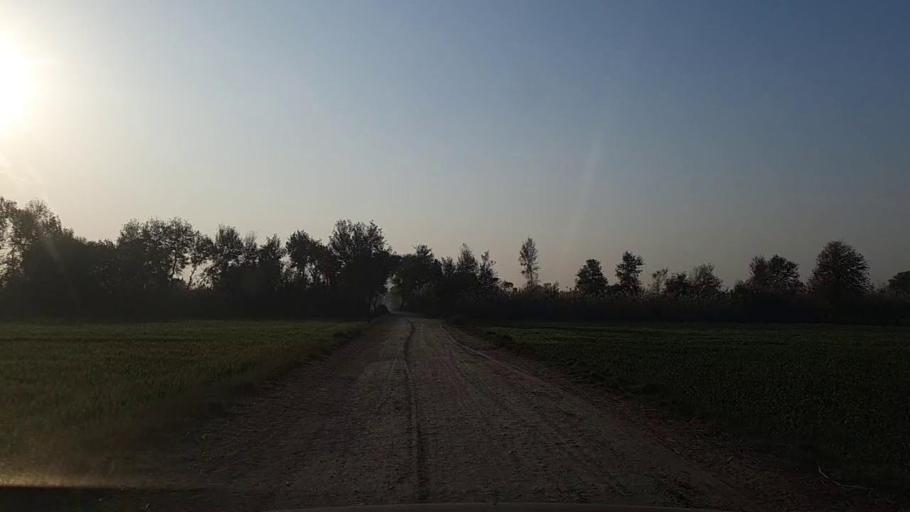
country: PK
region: Sindh
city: Daur
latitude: 26.4695
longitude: 68.3853
